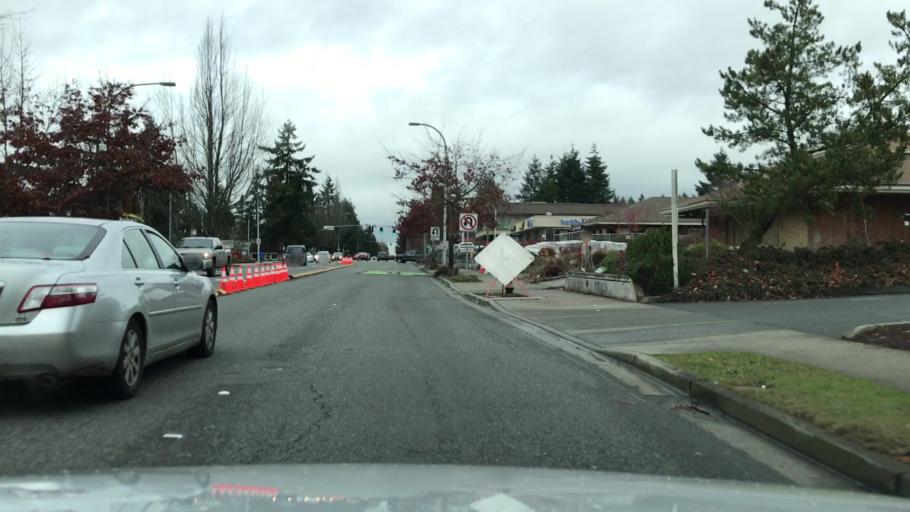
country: US
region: Washington
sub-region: King County
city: Eastgate
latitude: 47.6217
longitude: -122.1323
